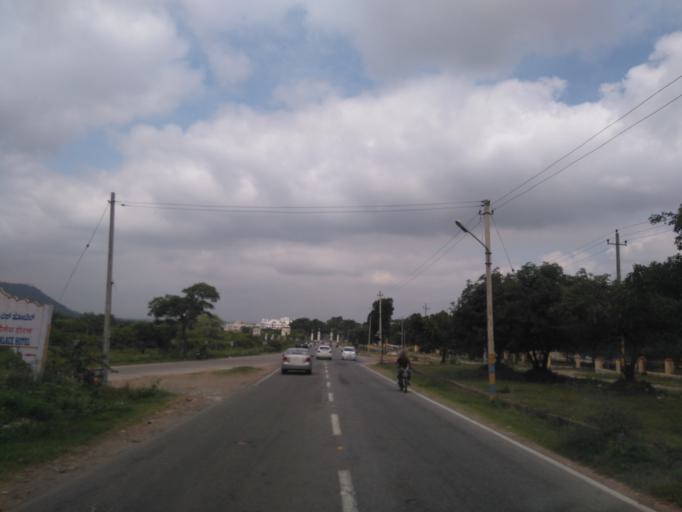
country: IN
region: Karnataka
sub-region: Mysore
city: Mysore
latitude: 12.3019
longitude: 76.6899
